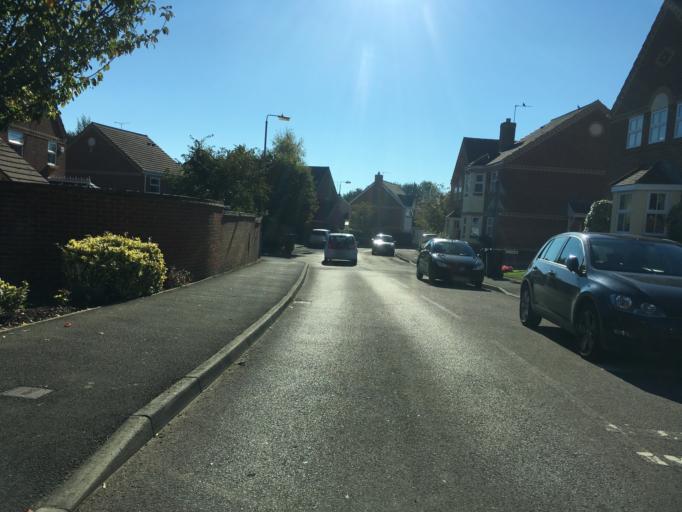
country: GB
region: England
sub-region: Wiltshire
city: Chippenham
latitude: 51.4695
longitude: -2.1392
